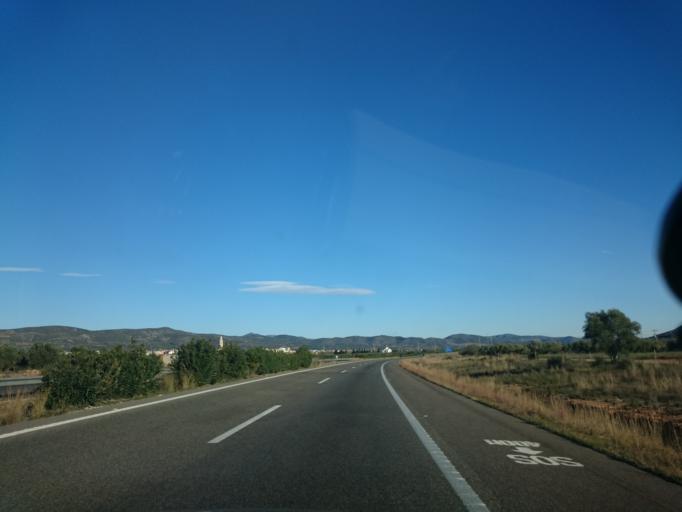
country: ES
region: Valencia
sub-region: Provincia de Castello
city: Alcala de Xivert
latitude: 40.2881
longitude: 0.2286
